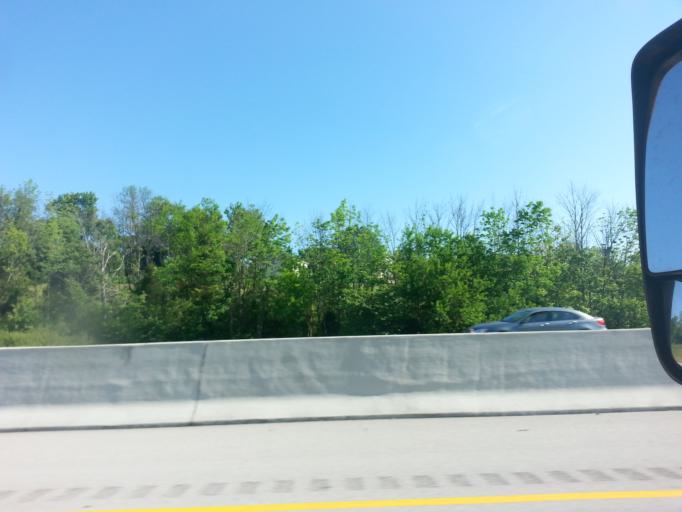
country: US
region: Kentucky
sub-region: Jefferson County
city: Middletown
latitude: 38.2213
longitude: -85.4613
